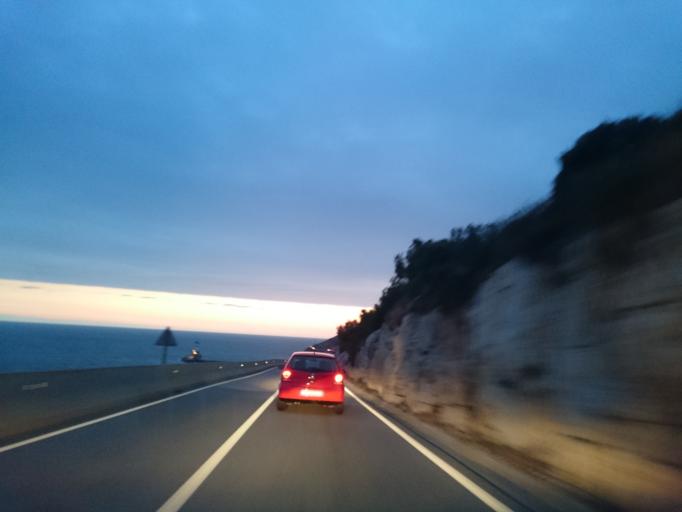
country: ES
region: Catalonia
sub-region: Provincia de Barcelona
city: Sitges
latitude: 41.2458
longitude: 1.8761
